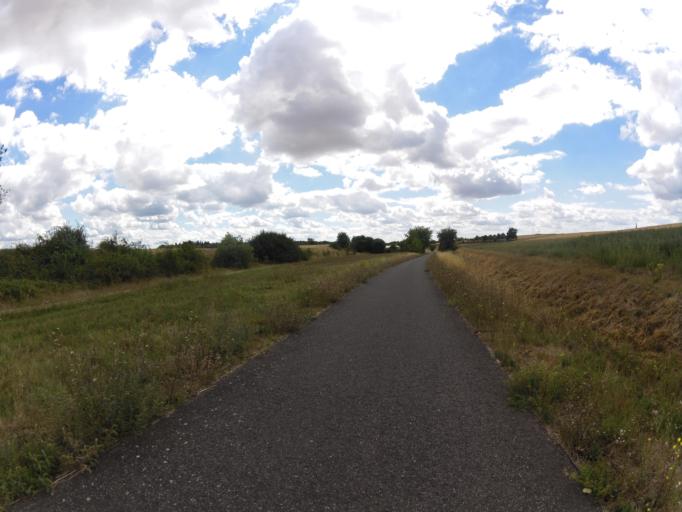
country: DE
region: Bavaria
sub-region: Regierungsbezirk Unterfranken
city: Aub
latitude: 49.5566
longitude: 10.0548
